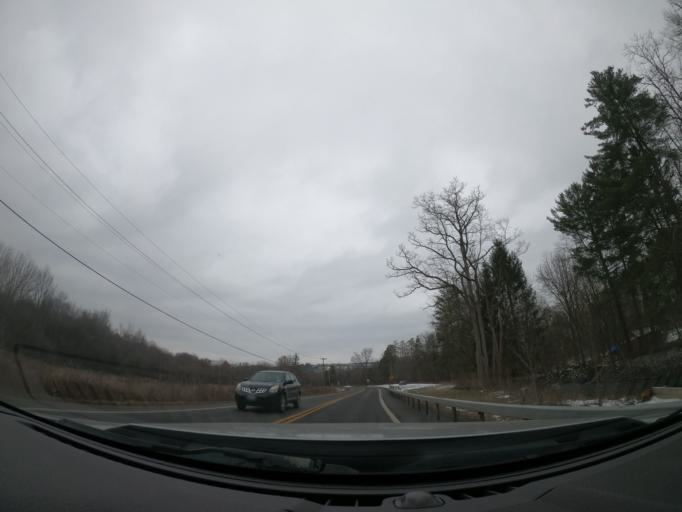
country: US
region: New York
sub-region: Cayuga County
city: Moravia
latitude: 42.6540
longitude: -76.4372
